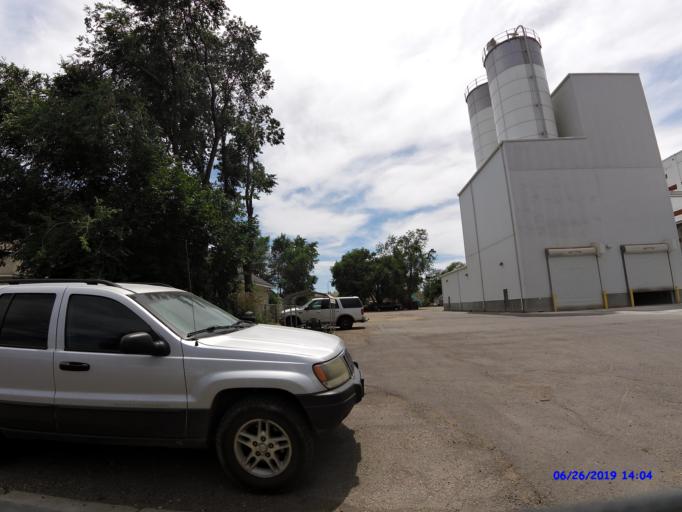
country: US
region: Utah
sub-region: Weber County
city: Ogden
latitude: 41.2103
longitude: -111.9825
